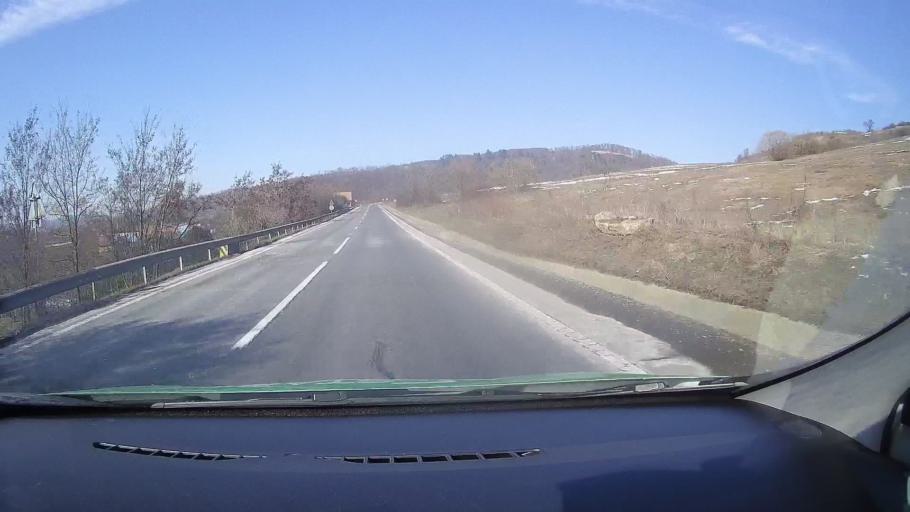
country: RO
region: Brasov
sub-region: Comuna Bunesti
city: Bunesti
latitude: 46.1502
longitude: 25.0293
